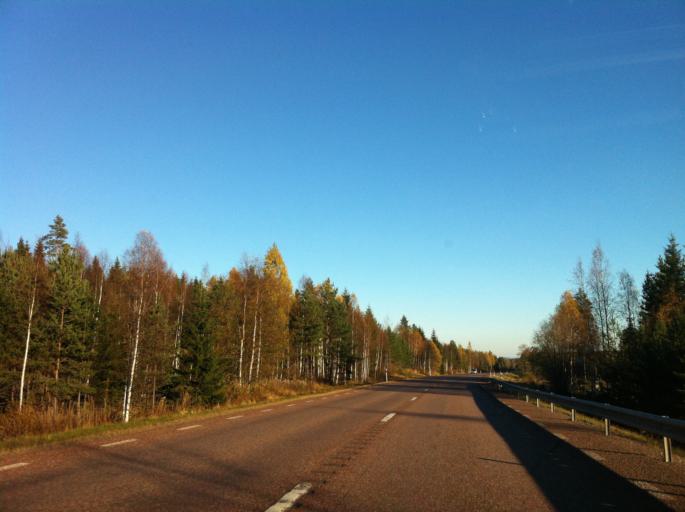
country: SE
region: Dalarna
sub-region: Faluns Kommun
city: Bjursas
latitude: 60.7461
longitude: 15.3687
